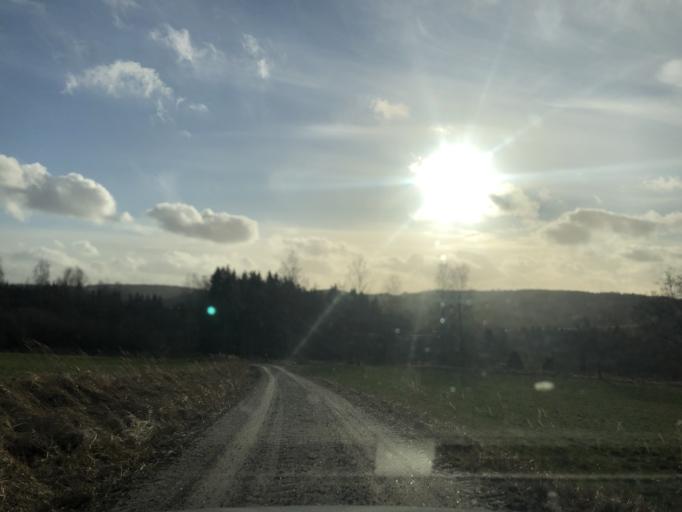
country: SE
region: Vaestra Goetaland
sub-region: Ulricehamns Kommun
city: Ulricehamn
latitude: 57.8196
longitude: 13.3651
